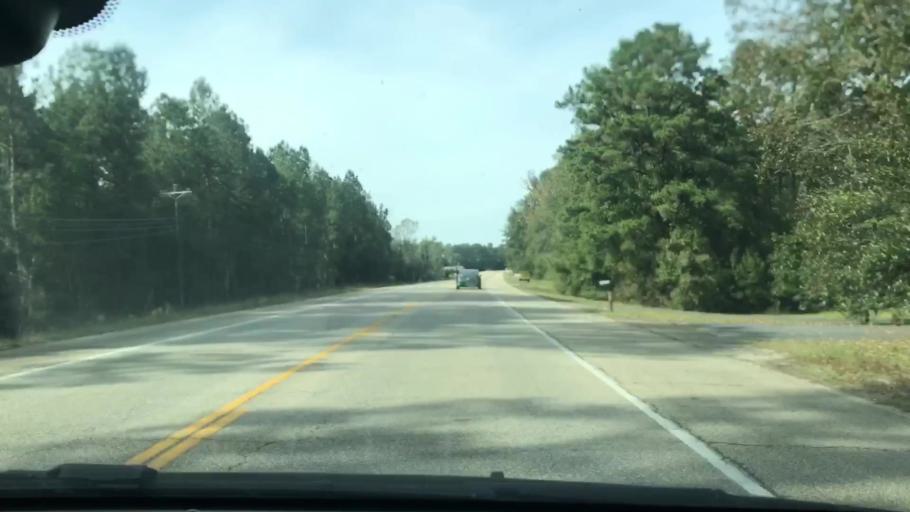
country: US
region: Louisiana
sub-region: Saint Tammany Parish
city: Pearl River
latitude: 30.4624
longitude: -89.8084
